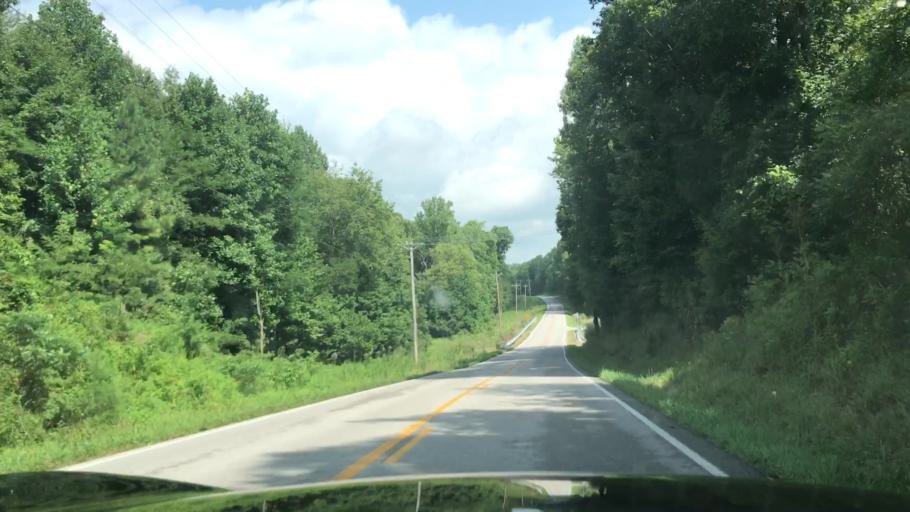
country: US
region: Kentucky
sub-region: Ohio County
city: Oak Grove
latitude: 37.1926
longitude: -86.8832
